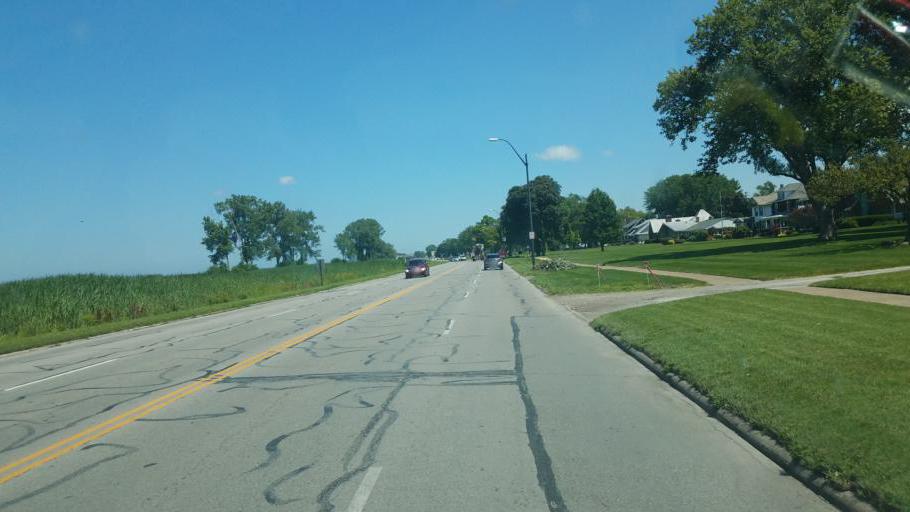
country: US
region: Ohio
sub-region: Ottawa County
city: Port Clinton
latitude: 41.5136
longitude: -82.9337
